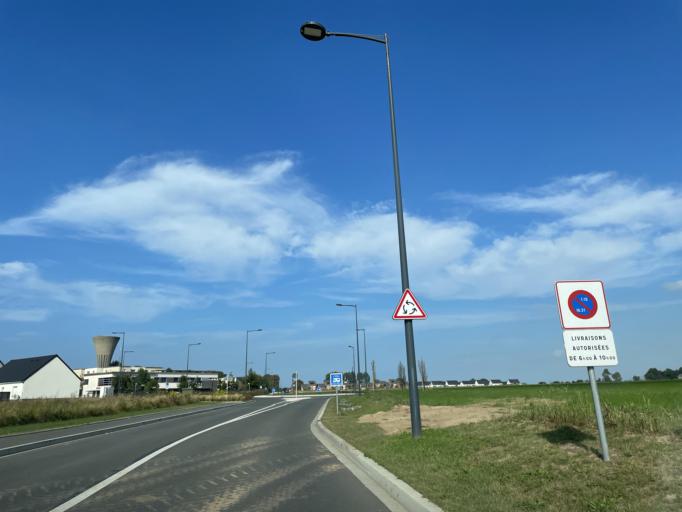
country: FR
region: Haute-Normandie
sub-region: Departement de la Seine-Maritime
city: Le Treport
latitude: 50.0460
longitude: 1.3659
